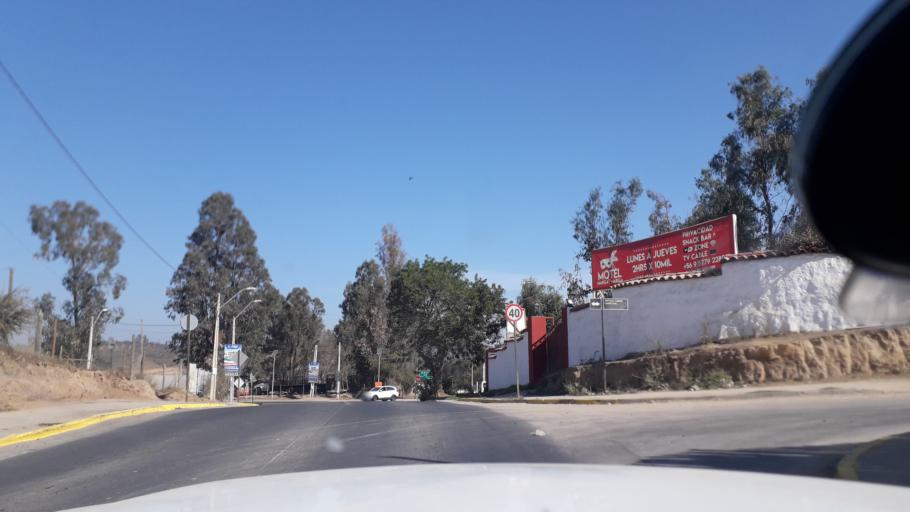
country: CL
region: Valparaiso
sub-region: Provincia de Marga Marga
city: Villa Alemana
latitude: -33.0715
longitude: -71.4048
